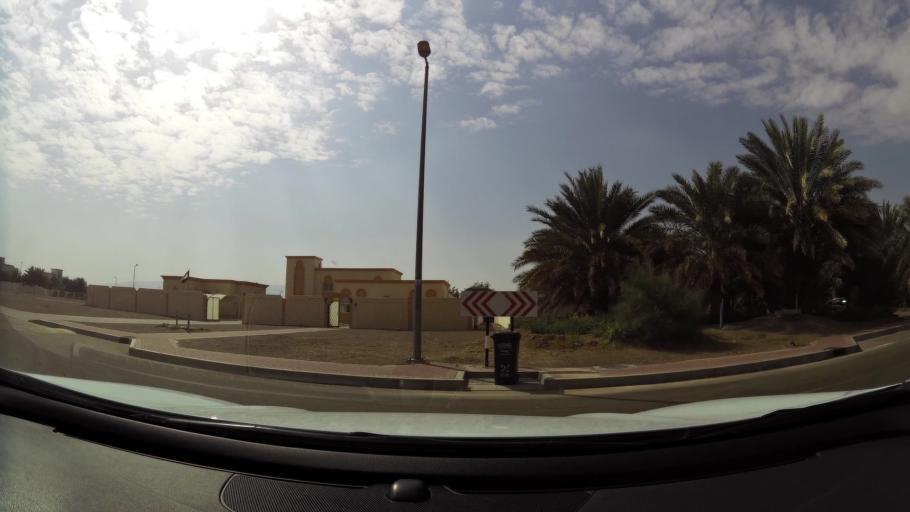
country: AE
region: Abu Dhabi
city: Al Ain
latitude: 24.0992
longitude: 55.8988
